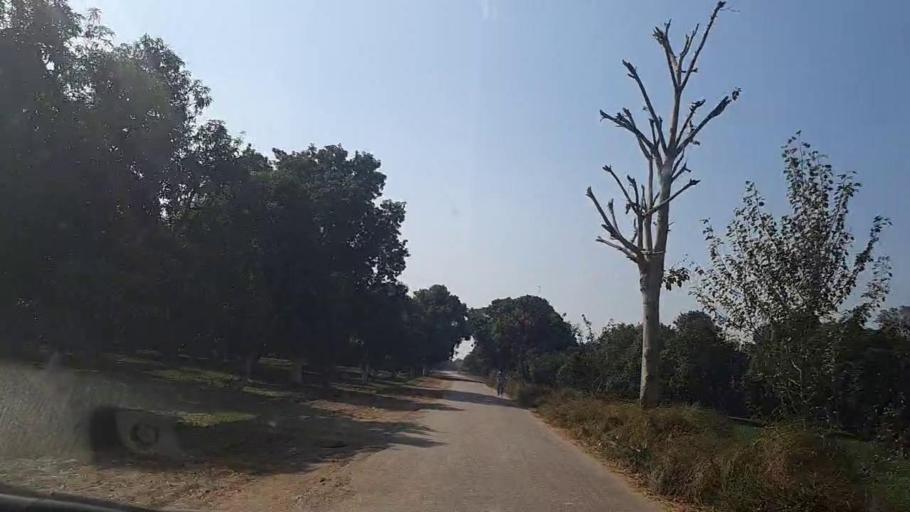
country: PK
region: Sindh
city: Sakrand
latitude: 26.0208
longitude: 68.3543
